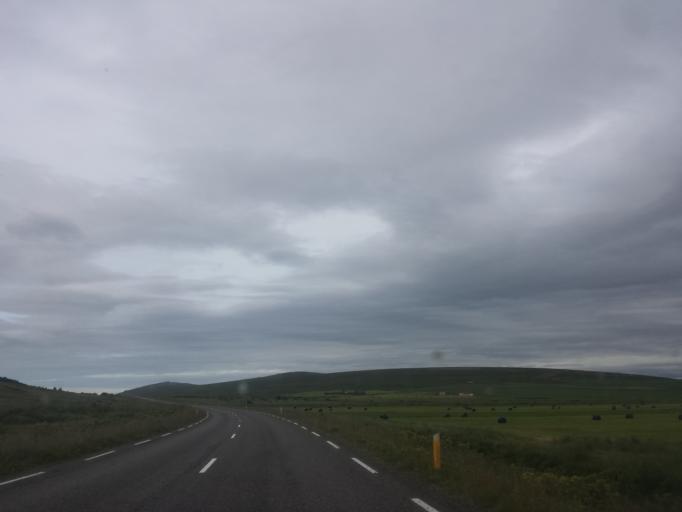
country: IS
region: Northeast
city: Laugar
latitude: 65.7146
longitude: -17.6020
